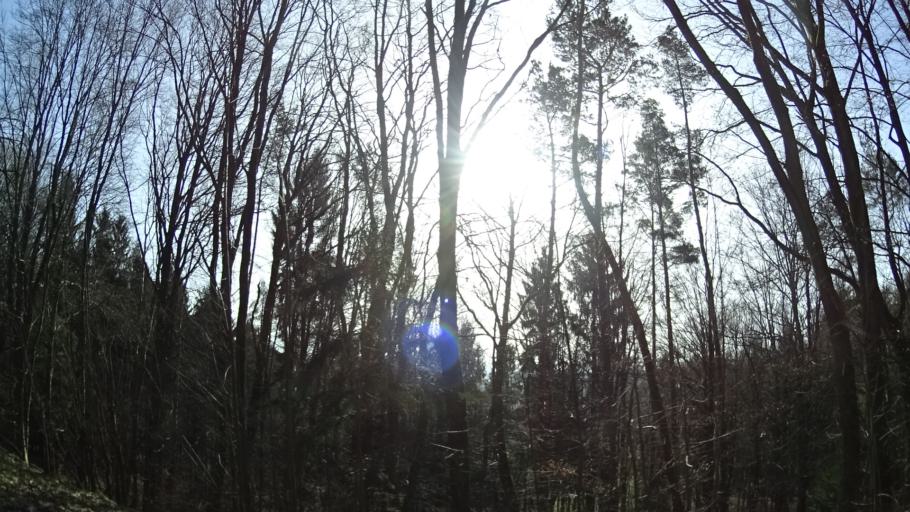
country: DE
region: Hesse
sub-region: Regierungsbezirk Darmstadt
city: Brensbach
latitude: 49.7165
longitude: 8.9239
